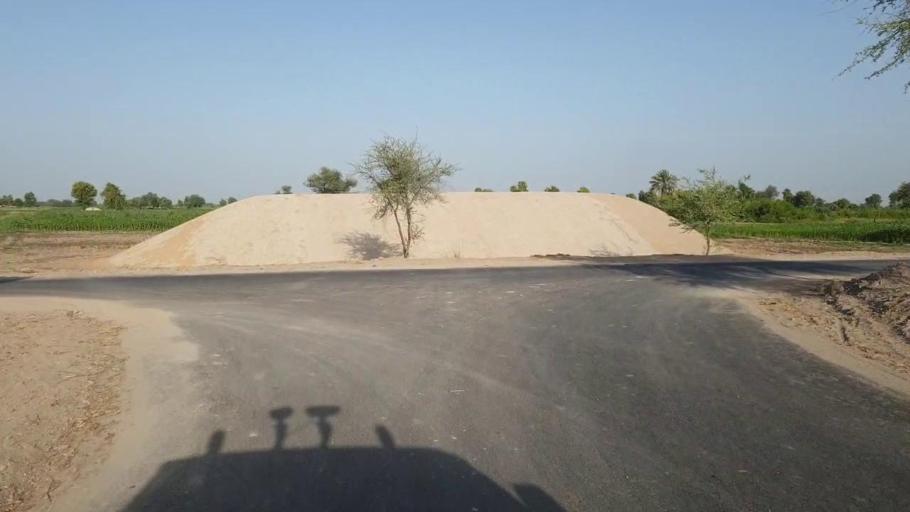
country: PK
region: Sindh
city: Jam Sahib
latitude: 26.3474
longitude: 68.5688
